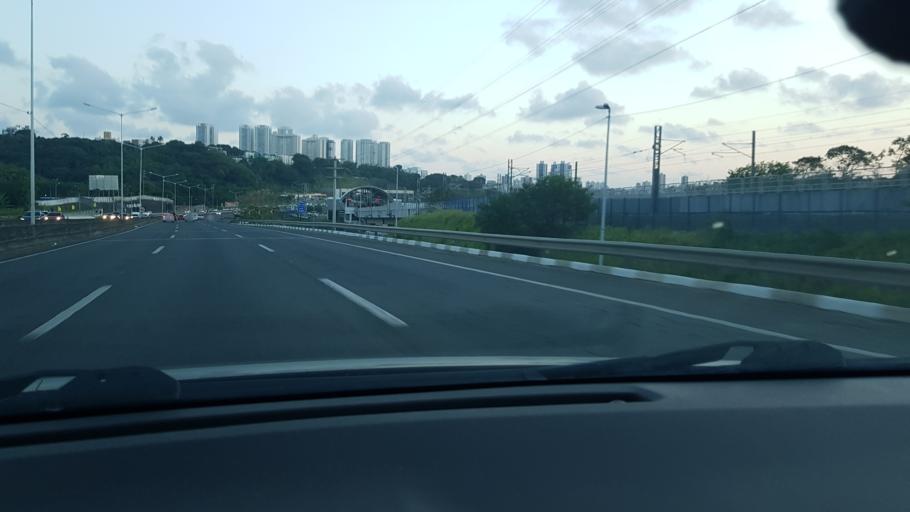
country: BR
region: Bahia
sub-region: Salvador
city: Salvador
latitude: -12.9528
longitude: -38.4713
